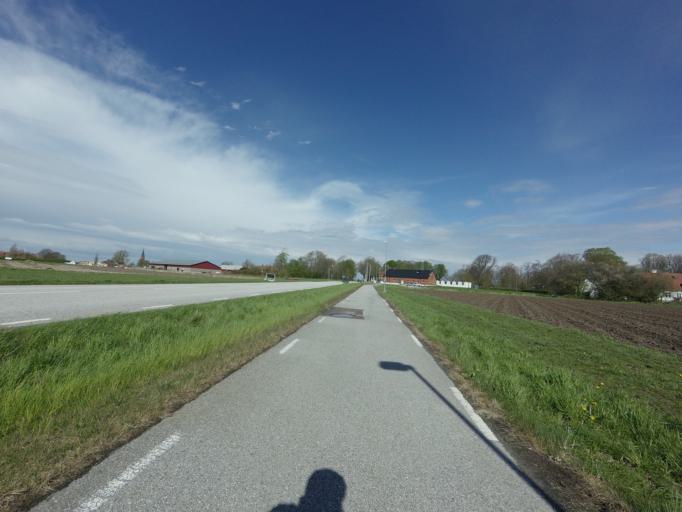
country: SE
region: Skane
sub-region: Malmo
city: Tygelsjo
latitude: 55.5000
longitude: 12.9979
